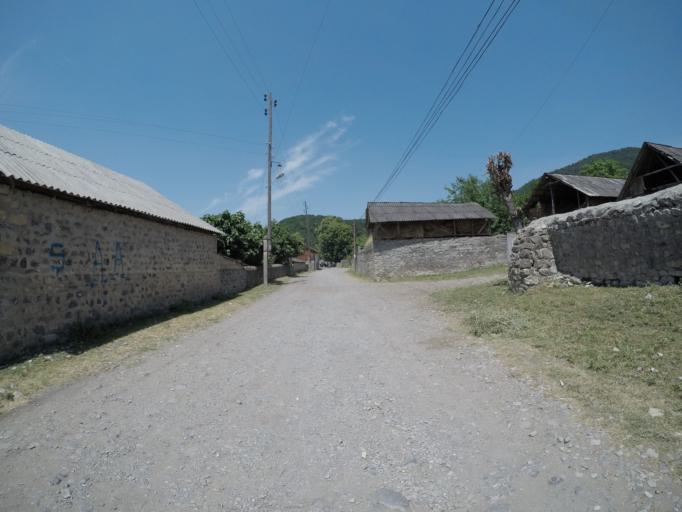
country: AZ
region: Qakh Rayon
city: Cinarli
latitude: 41.4840
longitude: 46.8462
